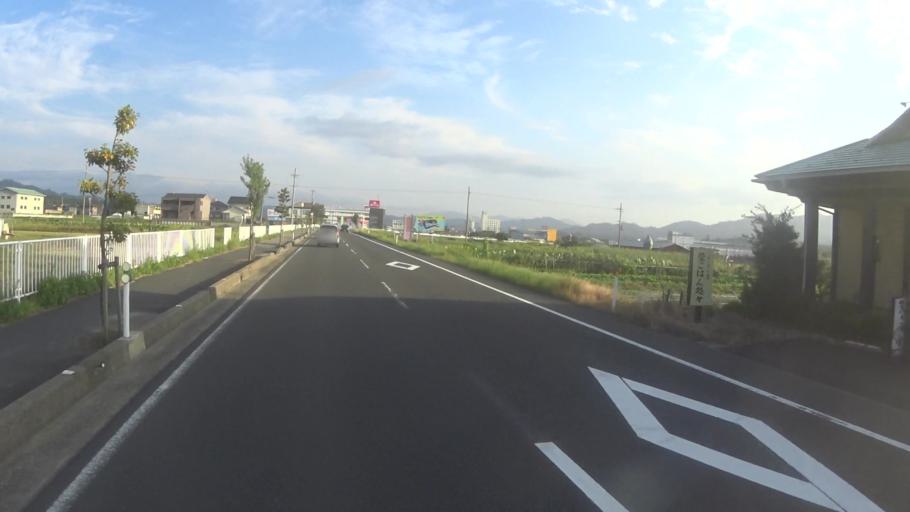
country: JP
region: Kyoto
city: Miyazu
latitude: 35.6131
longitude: 135.0792
